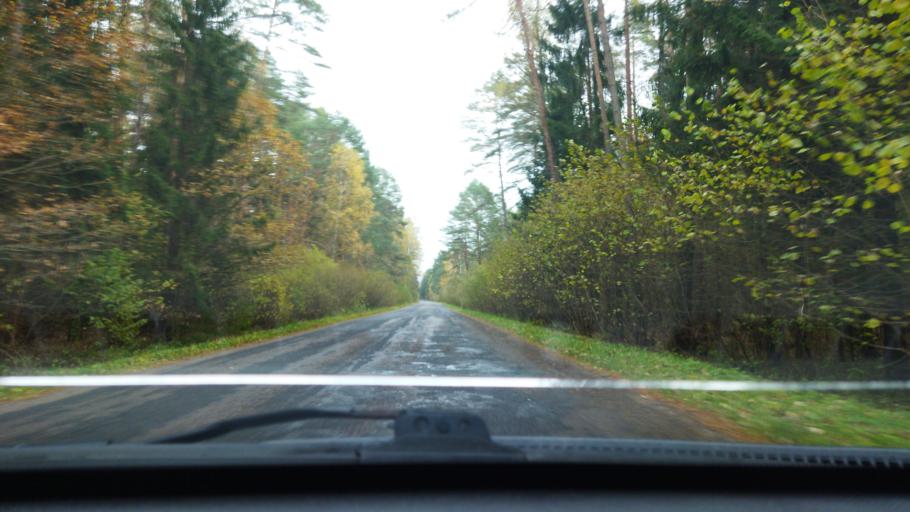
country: BY
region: Minsk
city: Svir
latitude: 54.8133
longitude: 26.1972
